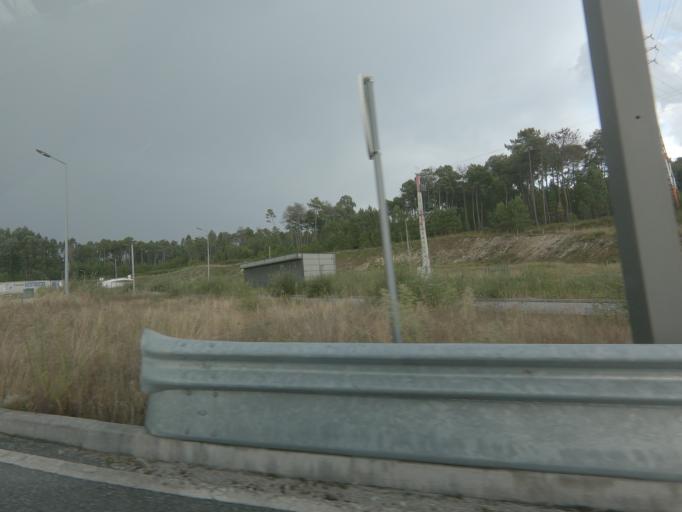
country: PT
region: Viseu
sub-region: Viseu
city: Campo
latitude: 40.7070
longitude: -7.9436
